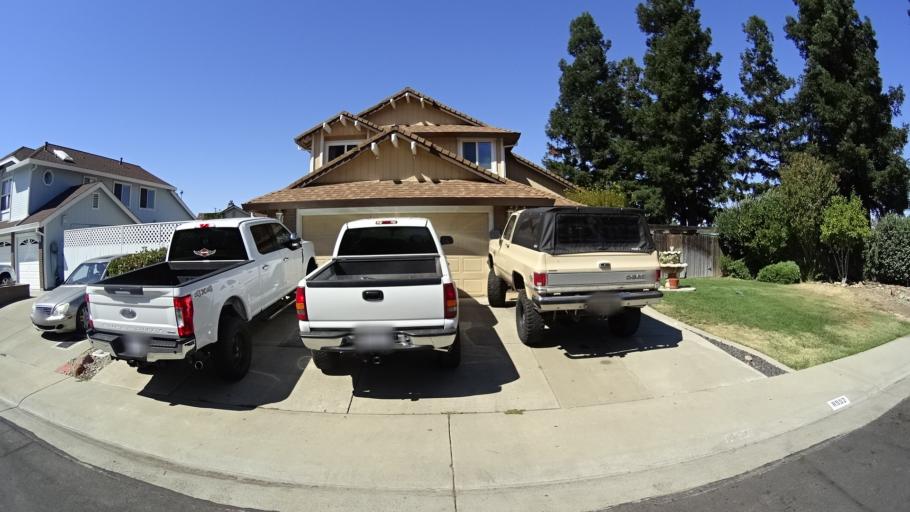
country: US
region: California
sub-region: Sacramento County
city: Laguna
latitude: 38.4305
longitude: -121.4369
